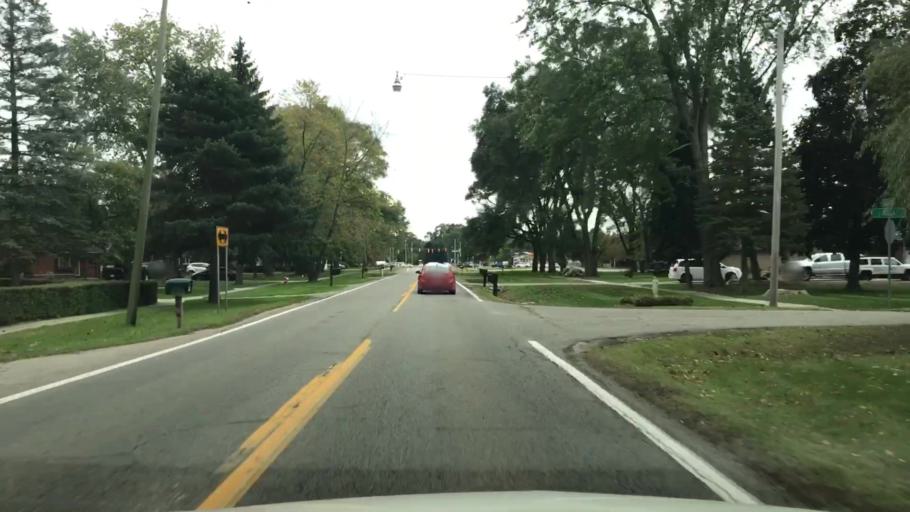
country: US
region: Michigan
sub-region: Macomb County
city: Shelby
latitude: 42.6715
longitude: -83.0643
